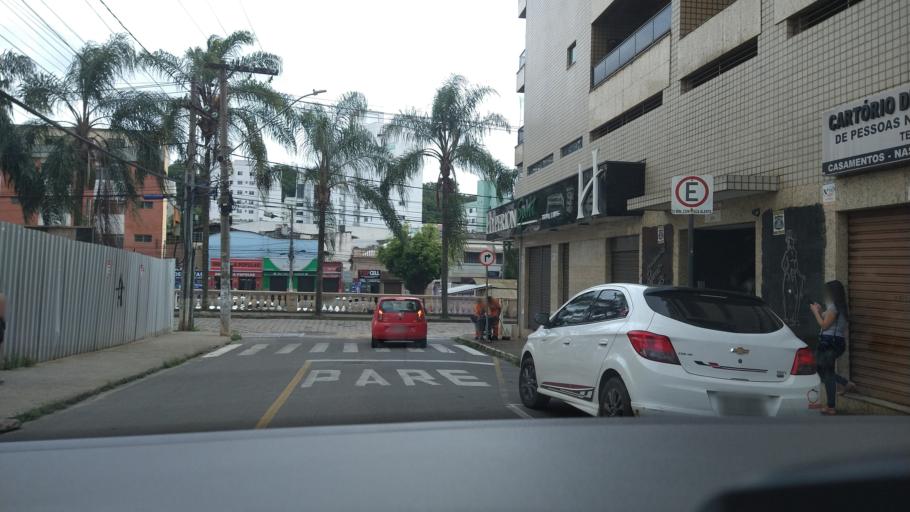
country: BR
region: Minas Gerais
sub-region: Vicosa
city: Vicosa
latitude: -20.7576
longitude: -42.8804
